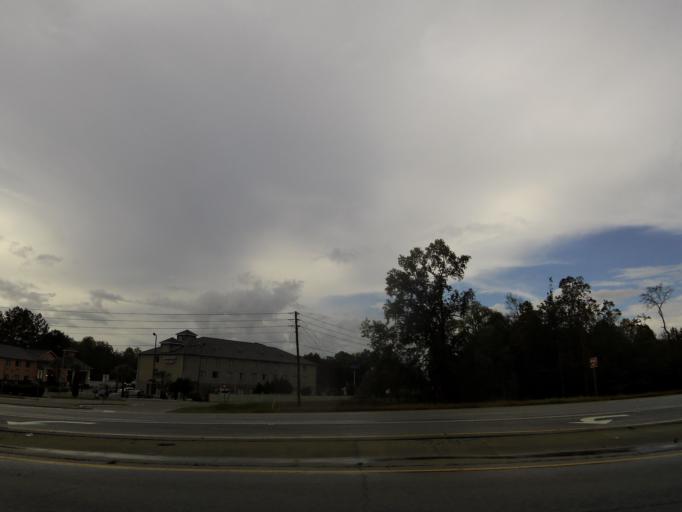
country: US
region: Georgia
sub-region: Wayne County
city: Jesup
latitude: 31.5968
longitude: -81.8683
